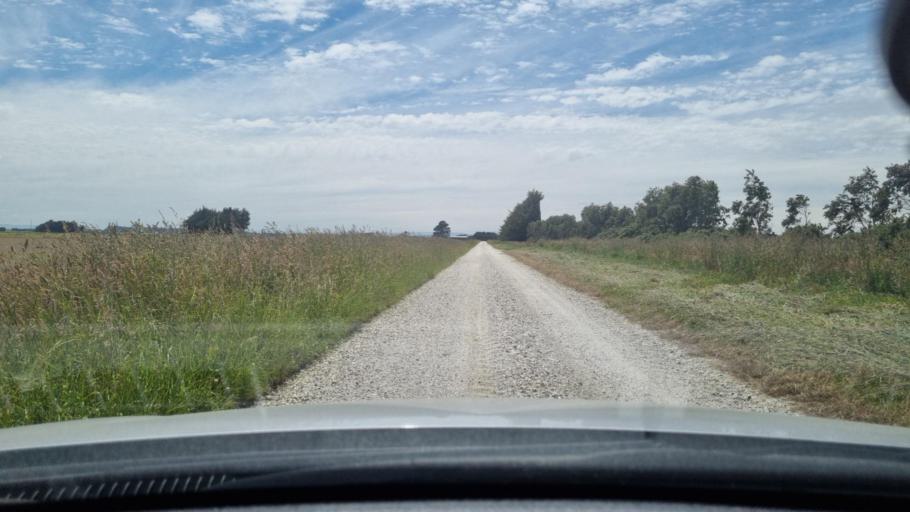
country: NZ
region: Southland
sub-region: Invercargill City
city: Invercargill
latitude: -46.3735
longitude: 168.2761
